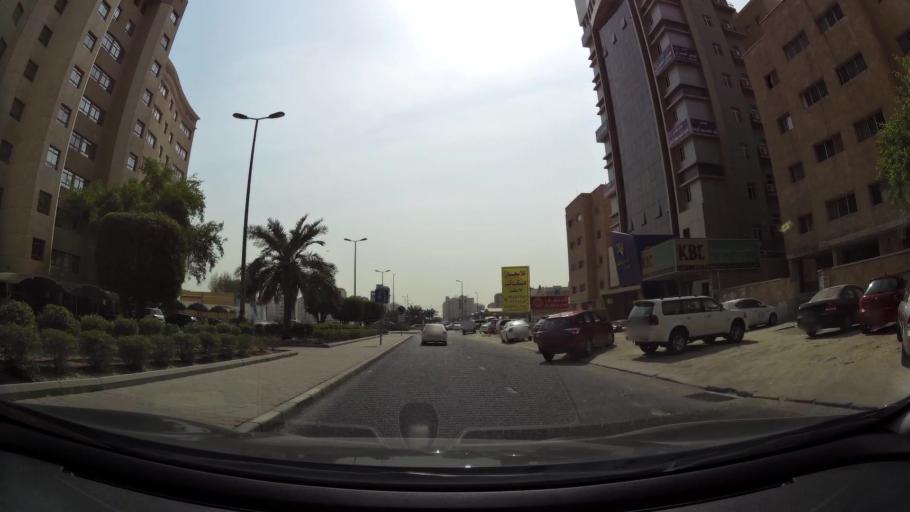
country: KW
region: Al Asimah
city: Ar Rabiyah
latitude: 29.3065
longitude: 47.9148
